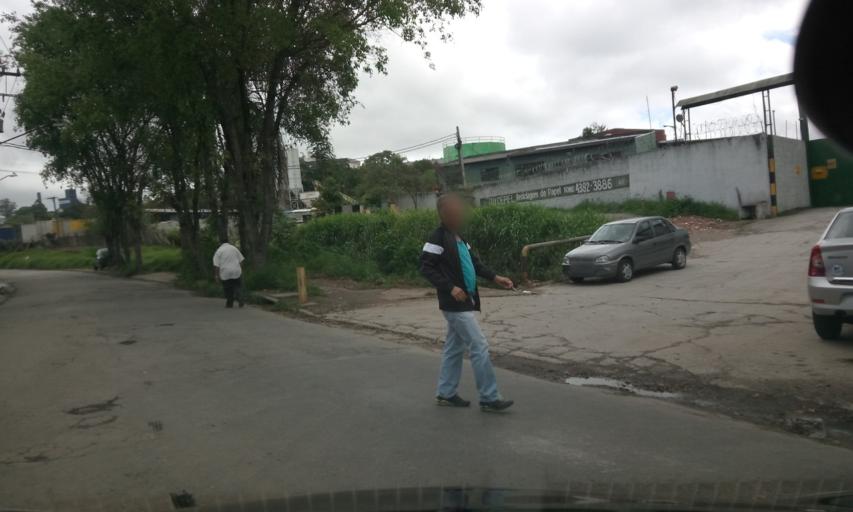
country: BR
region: Sao Paulo
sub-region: Sao Bernardo Do Campo
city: Sao Bernardo do Campo
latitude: -23.7091
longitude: -46.5930
